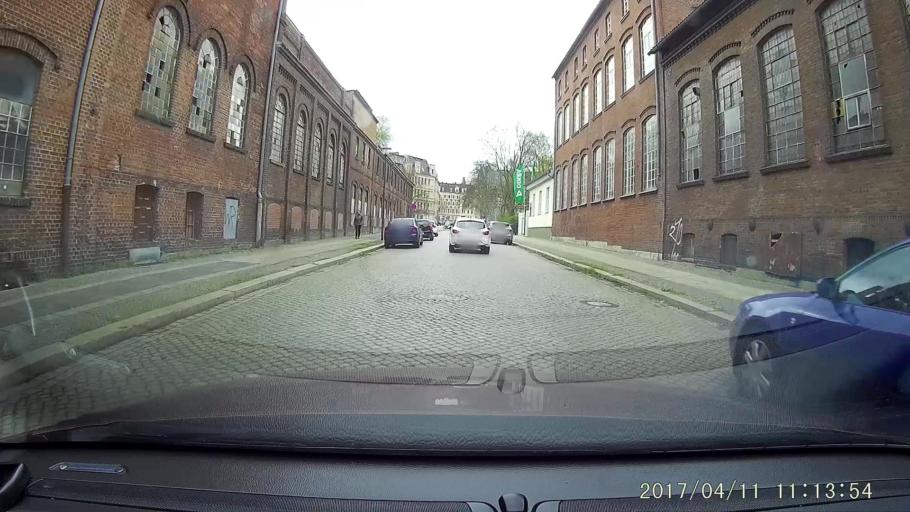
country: DE
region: Saxony
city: Goerlitz
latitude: 51.1543
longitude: 14.9757
